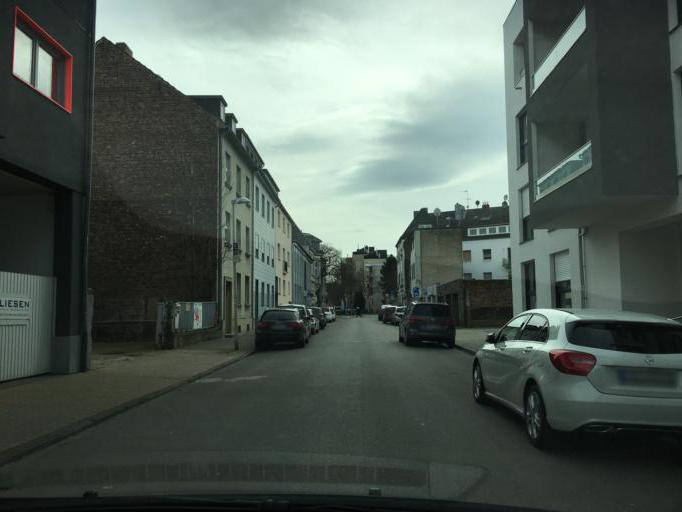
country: DE
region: North Rhine-Westphalia
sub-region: Regierungsbezirk Koln
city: Dueren
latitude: 50.8006
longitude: 6.4890
